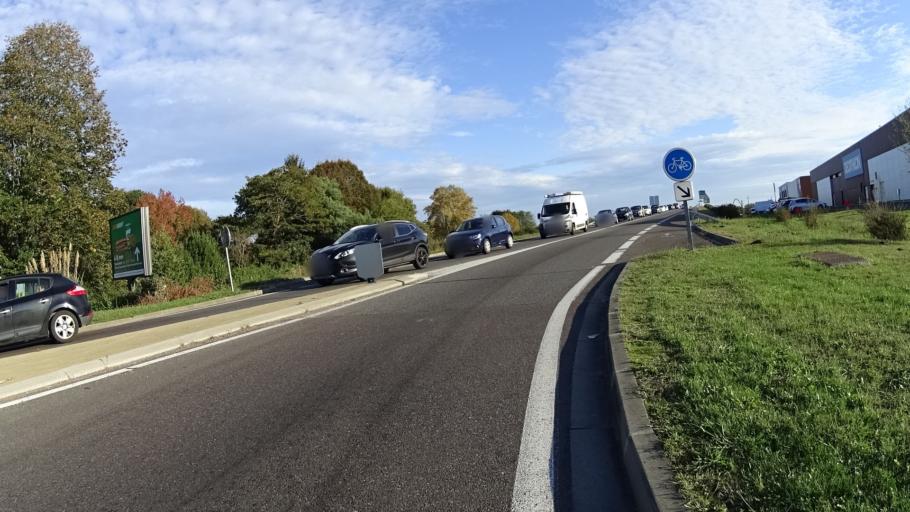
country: FR
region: Aquitaine
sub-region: Departement des Landes
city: Saint-Paul-les-Dax
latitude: 43.7296
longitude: -1.0380
